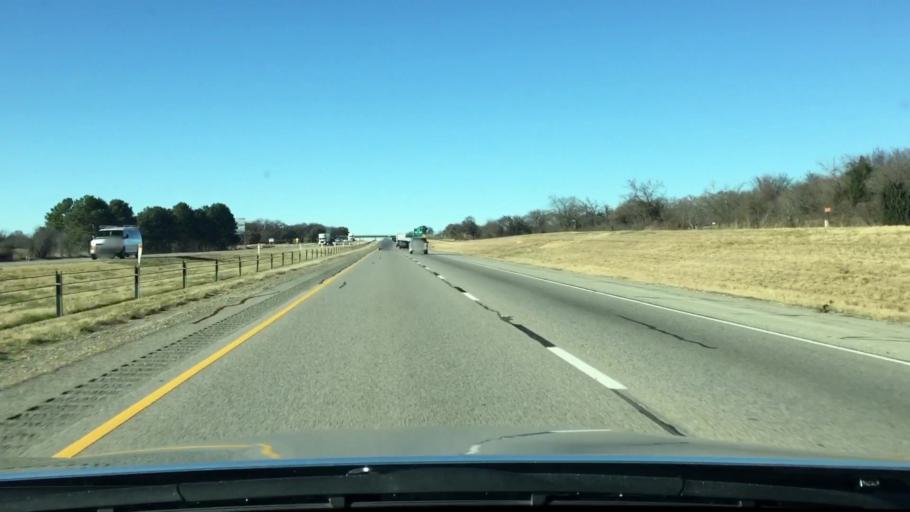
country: US
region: Texas
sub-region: Johnson County
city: Alvarado
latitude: 32.3738
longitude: -97.2033
